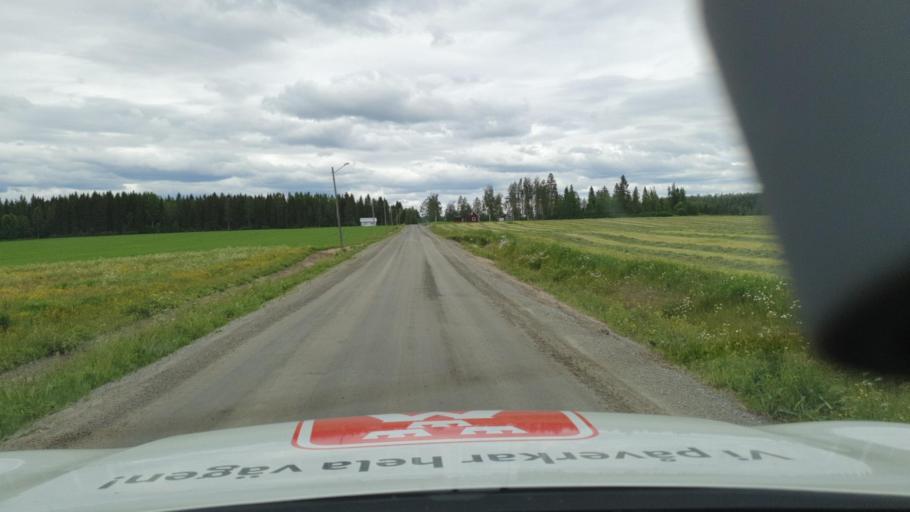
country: SE
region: Vaesterbotten
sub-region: Nordmalings Kommun
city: Nordmaling
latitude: 63.6995
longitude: 19.4423
